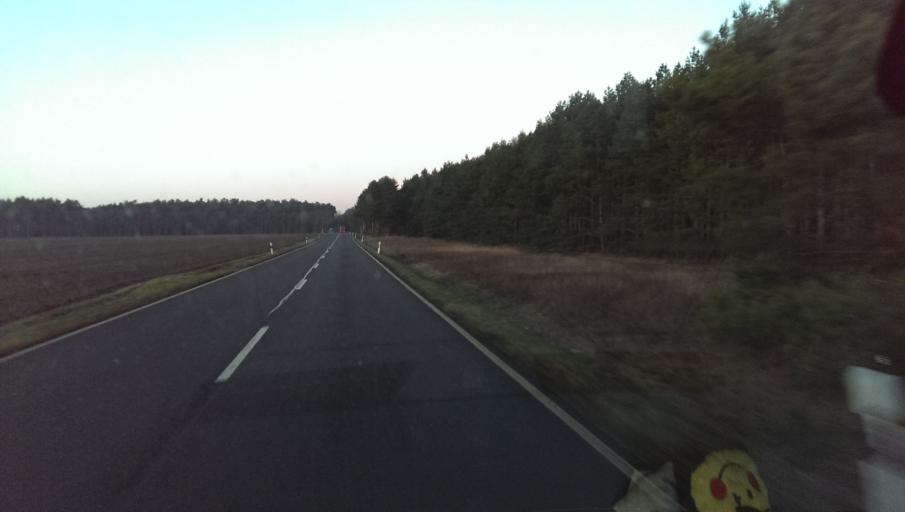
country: DE
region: Saxony-Anhalt
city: Holzdorf
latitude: 51.8552
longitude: 13.1471
